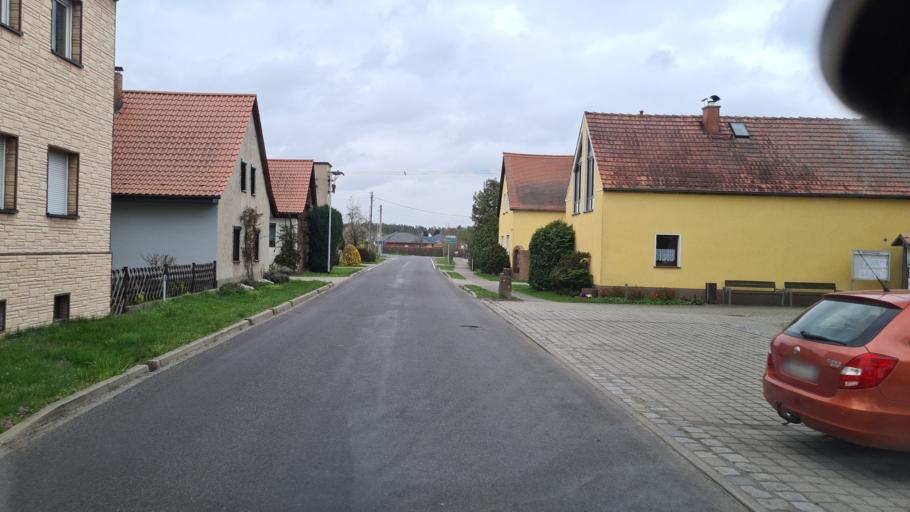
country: DE
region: Brandenburg
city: Schwarzbach
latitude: 51.4524
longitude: 13.9349
